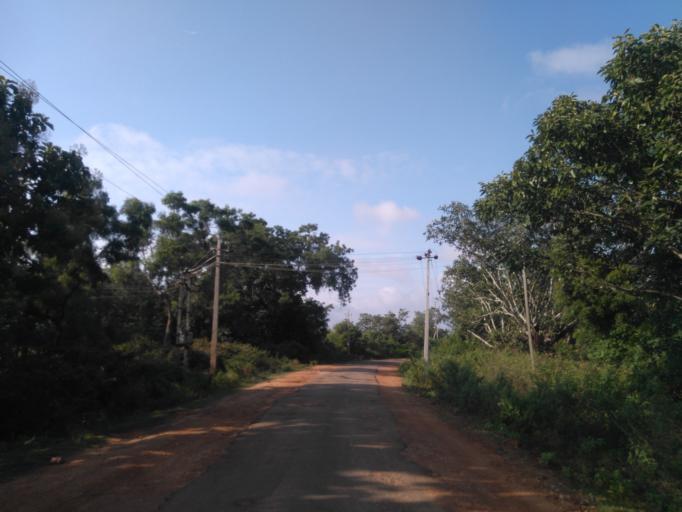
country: IN
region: Karnataka
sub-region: Chamrajnagar
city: Kollegal
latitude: 12.2642
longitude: 77.0648
